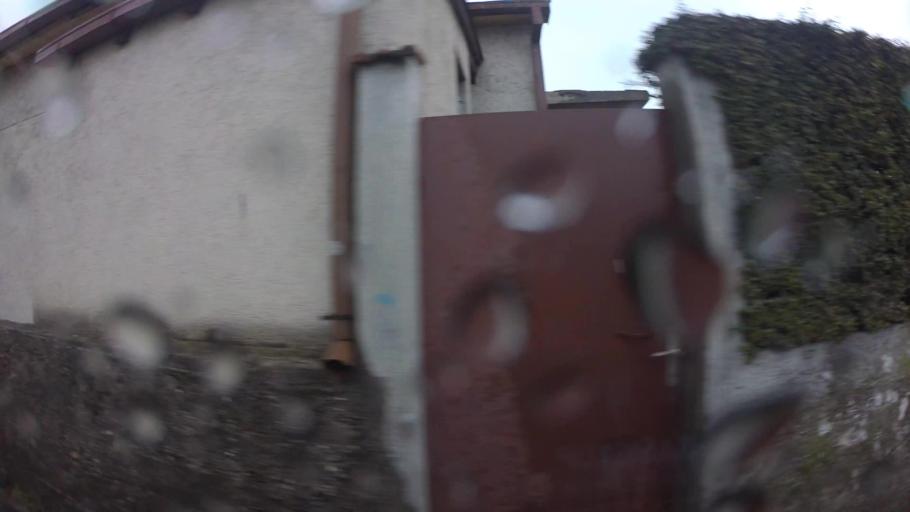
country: BA
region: Federation of Bosnia and Herzegovina
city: Cim
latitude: 43.3485
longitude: 17.7809
